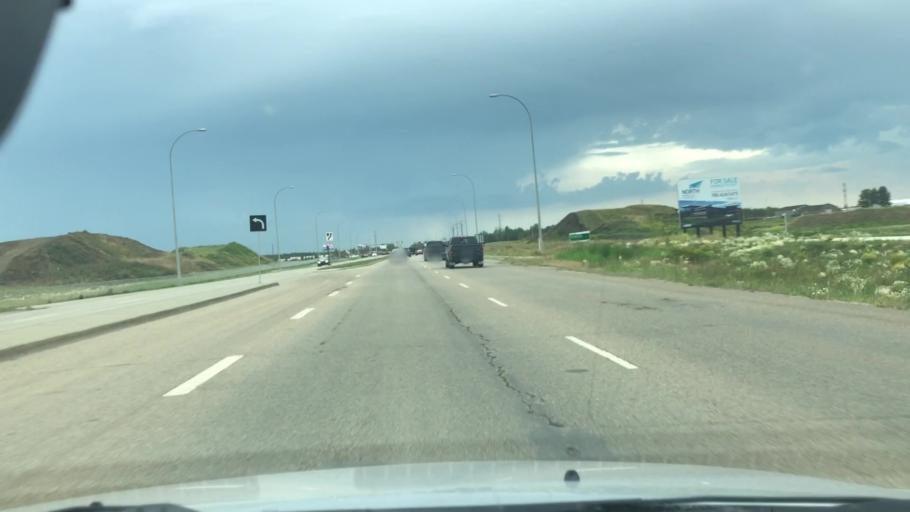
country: CA
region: Alberta
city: St. Albert
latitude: 53.5994
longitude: -113.6075
